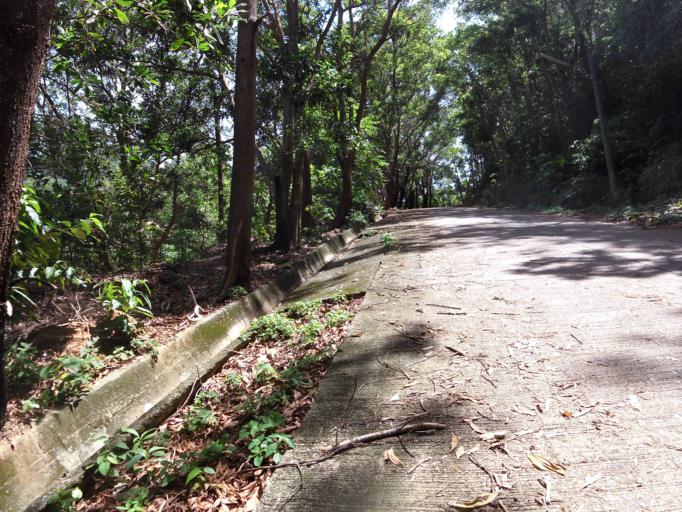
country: TH
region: Phuket
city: Ban Karon
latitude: 7.8471
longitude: 98.3022
